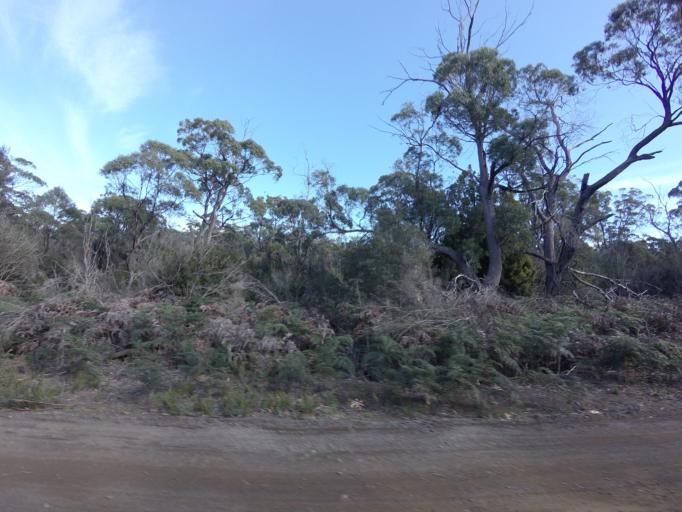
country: AU
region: Tasmania
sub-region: Clarence
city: Sandford
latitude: -42.9894
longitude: 147.7142
